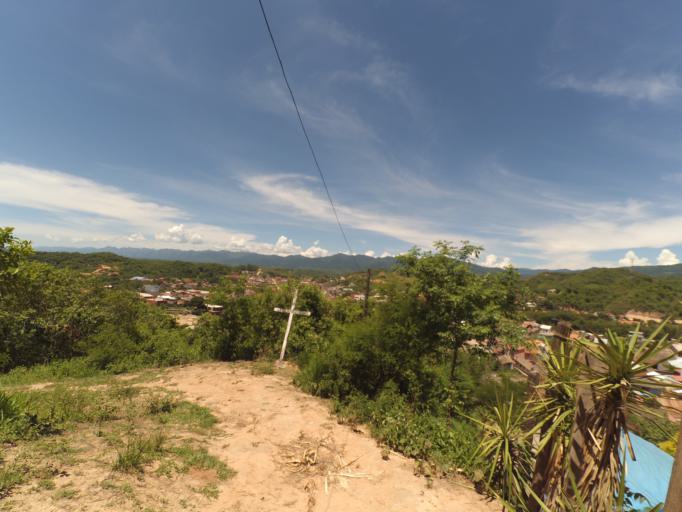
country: BO
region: Chuquisaca
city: Monteagudo
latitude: -19.8026
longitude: -63.9534
